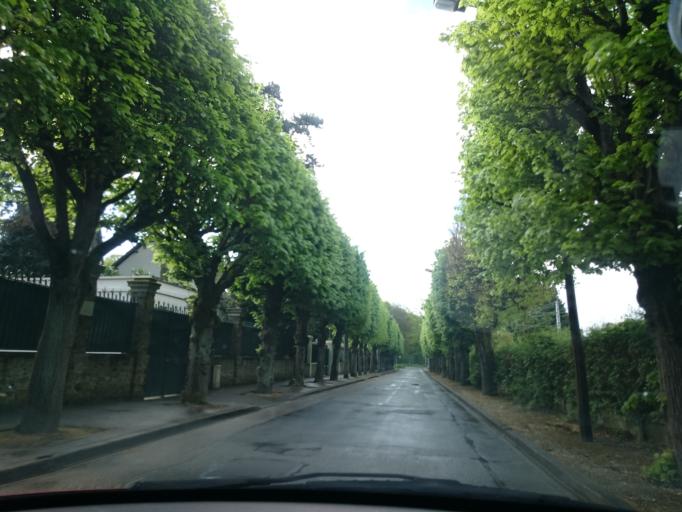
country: FR
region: Ile-de-France
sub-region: Departement de l'Essonne
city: Evry
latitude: 48.6363
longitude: 2.4498
